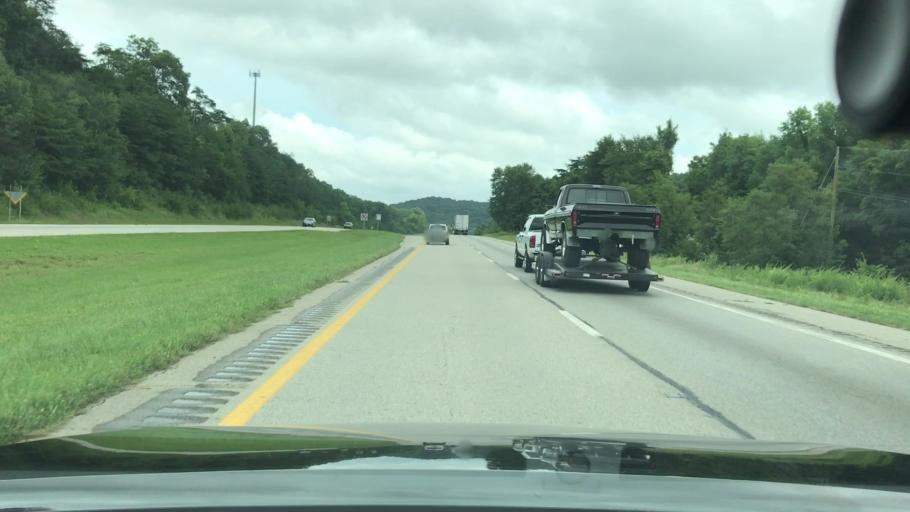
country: US
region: Ohio
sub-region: Jackson County
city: Jackson
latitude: 39.0812
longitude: -82.6372
